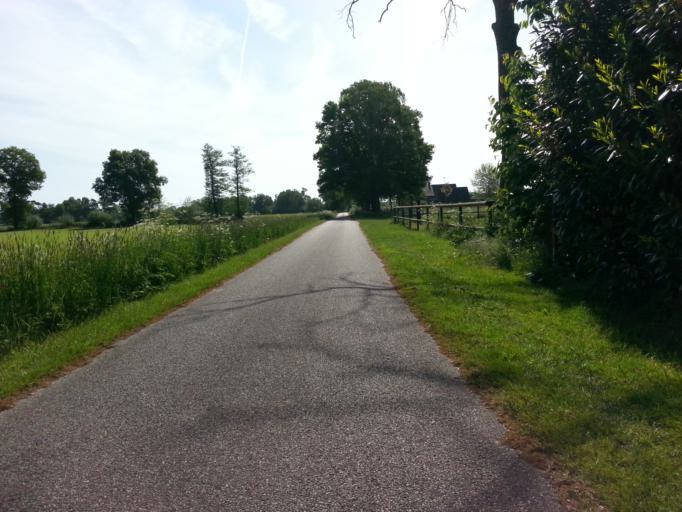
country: NL
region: Gelderland
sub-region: Berkelland
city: Eibergen
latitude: 52.1295
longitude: 6.6533
